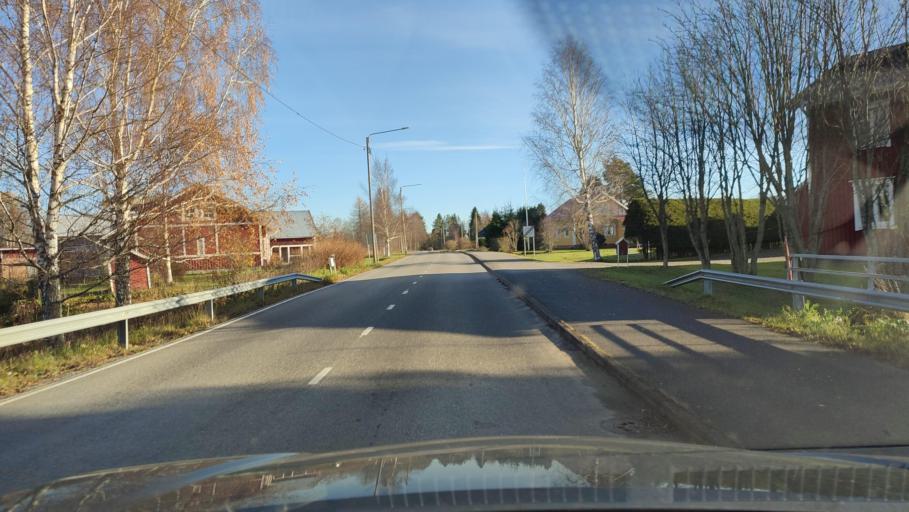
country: FI
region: Southern Ostrobothnia
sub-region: Suupohja
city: Teuva
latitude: 62.4886
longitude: 21.7566
